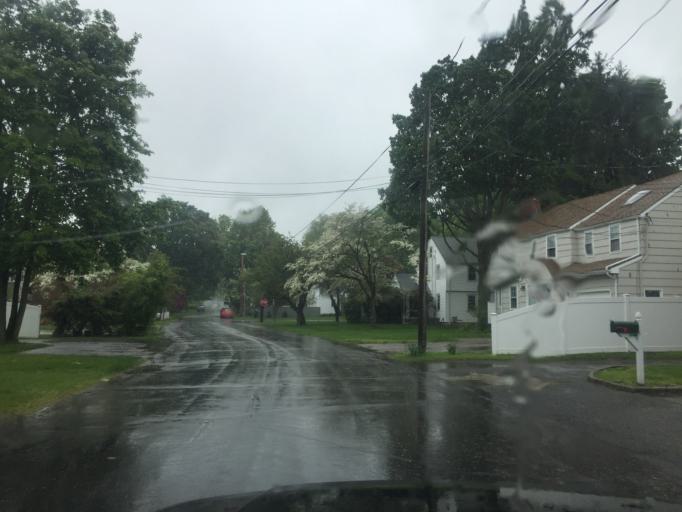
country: US
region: Connecticut
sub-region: Fairfield County
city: Fairfield
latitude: 41.1395
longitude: -73.2707
